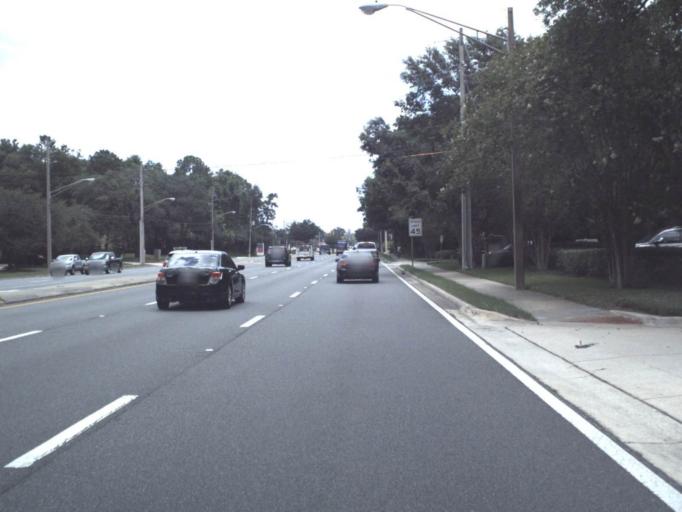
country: US
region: Florida
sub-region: Saint Johns County
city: Fruit Cove
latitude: 30.1536
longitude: -81.6325
